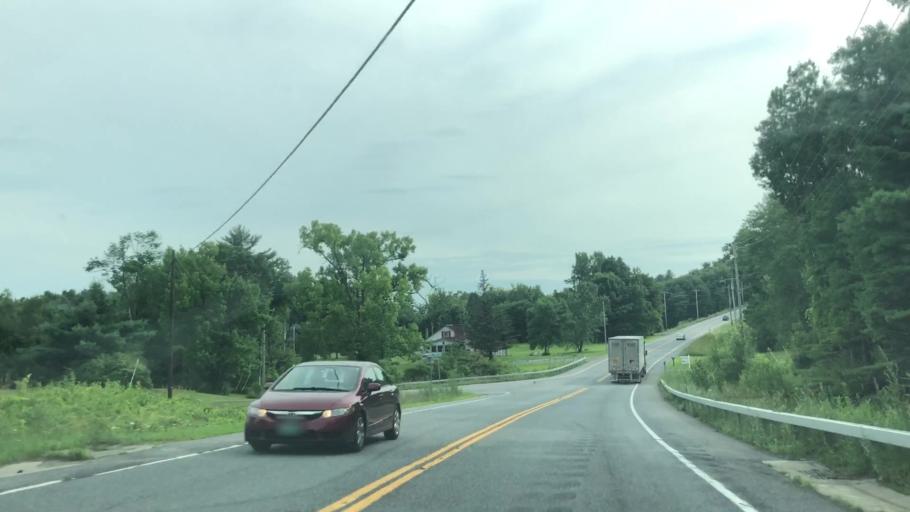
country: US
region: New York
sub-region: Warren County
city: Queensbury
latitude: 43.3789
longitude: -73.6600
